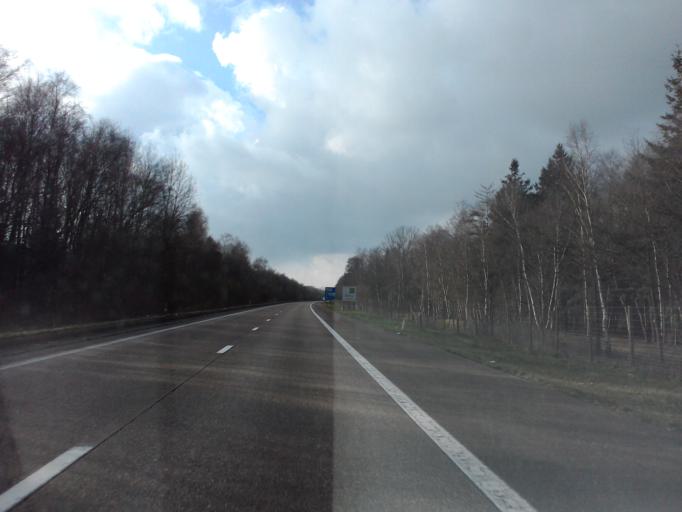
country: BE
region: Flanders
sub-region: Provincie Antwerpen
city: Arendonk
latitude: 51.2967
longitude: 5.1252
